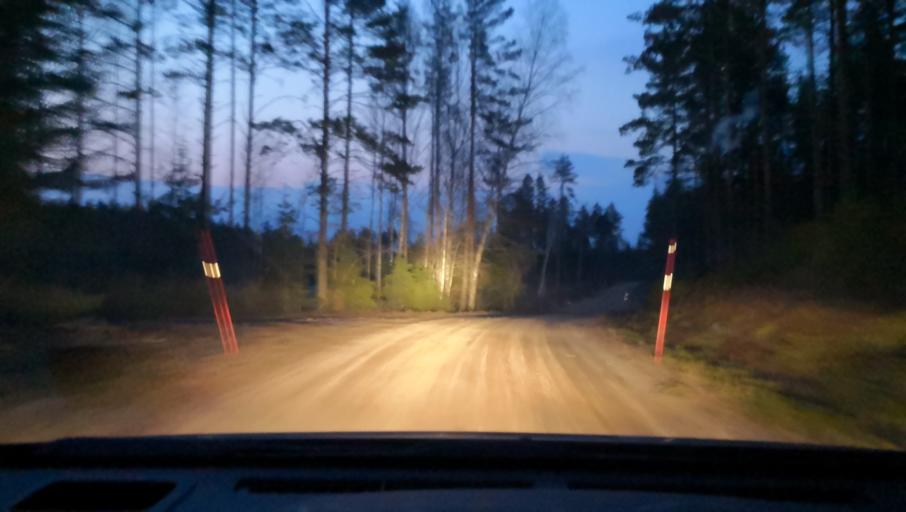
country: SE
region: OErebro
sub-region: Lindesbergs Kommun
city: Frovi
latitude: 59.5970
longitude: 15.4663
